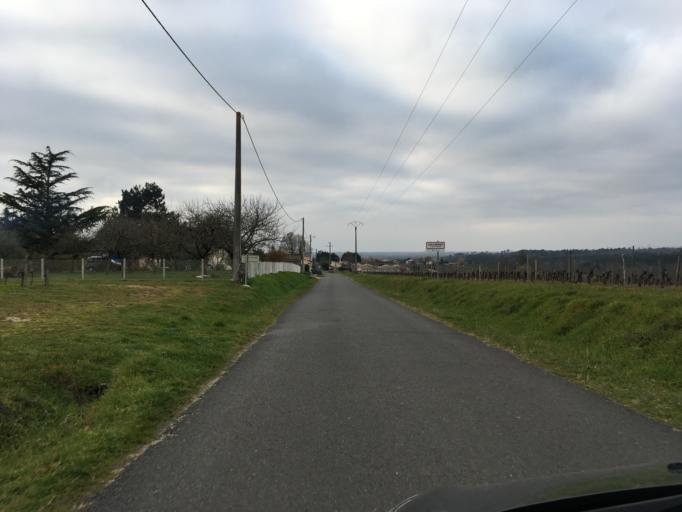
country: FR
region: Aquitaine
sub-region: Departement de la Gironde
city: Saint-Ciers-sur-Gironde
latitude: 45.3123
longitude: -0.6078
